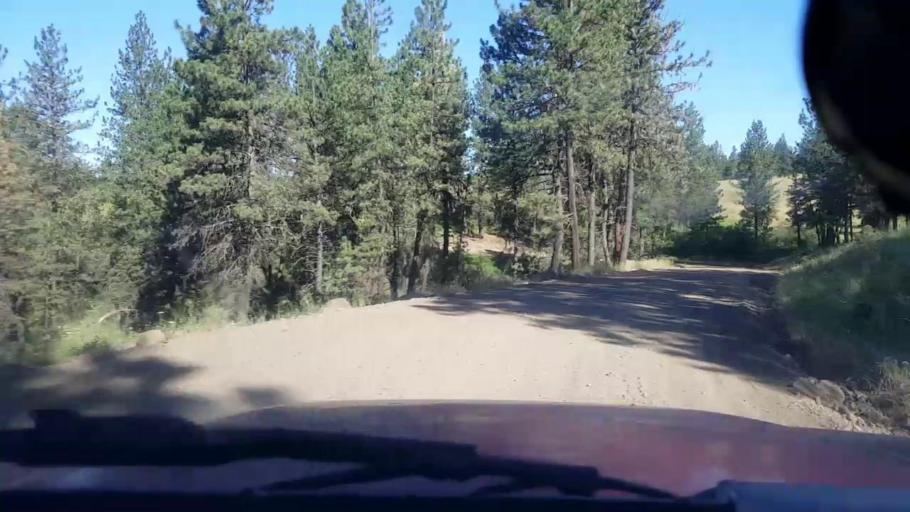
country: US
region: Washington
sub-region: Garfield County
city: Pomeroy
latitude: 45.9846
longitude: -117.4709
